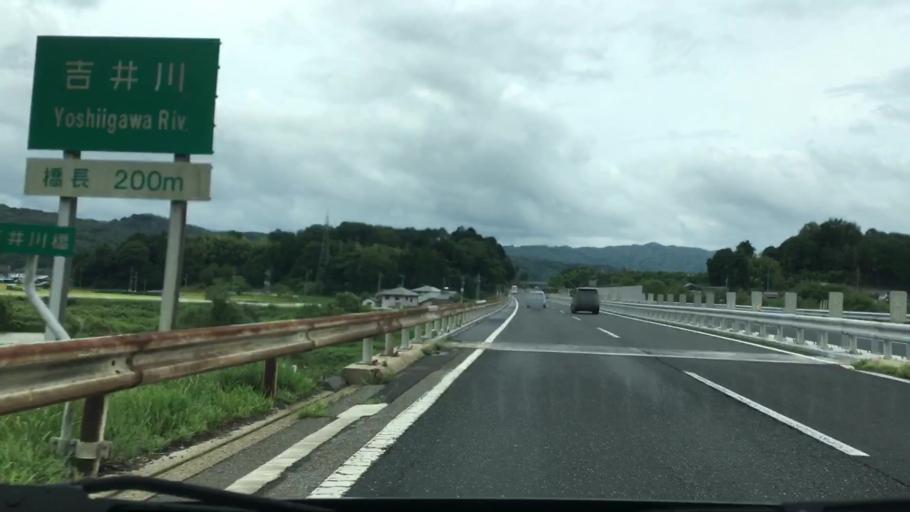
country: JP
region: Okayama
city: Tsuyama
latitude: 35.0617
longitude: 133.9350
